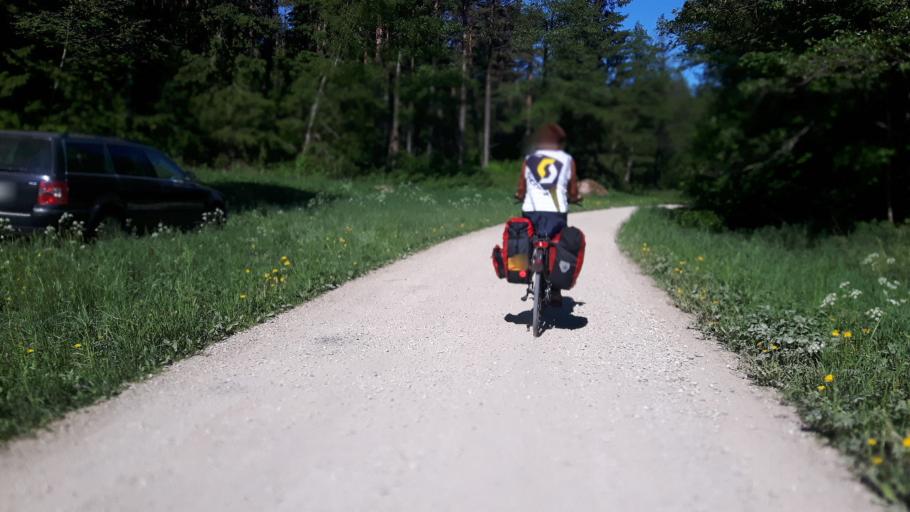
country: EE
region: Harju
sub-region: Loksa linn
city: Loksa
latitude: 59.5634
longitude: 25.8584
